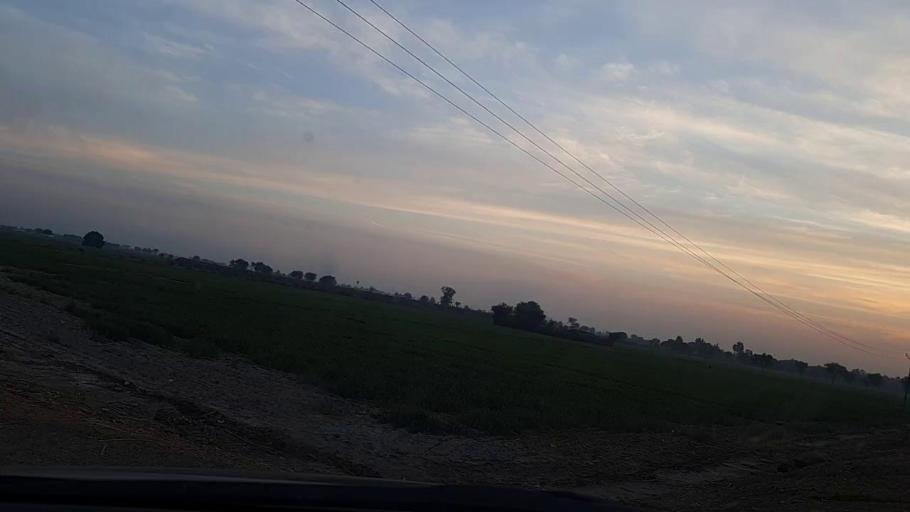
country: PK
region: Sindh
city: Sakrand
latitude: 26.2039
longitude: 68.3166
